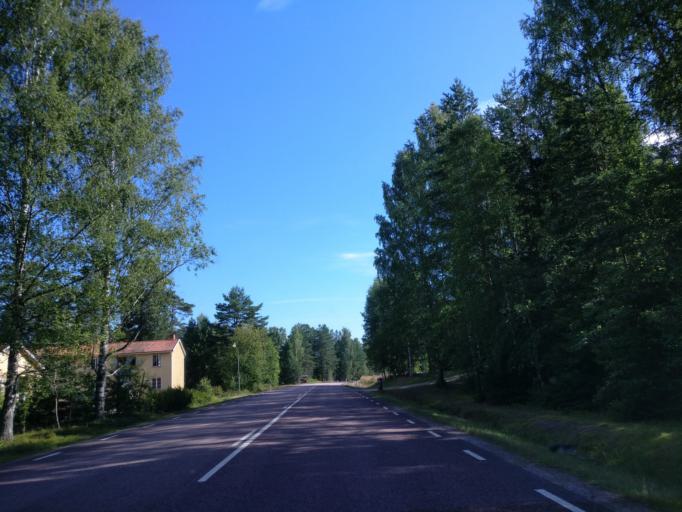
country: SE
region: Vaermland
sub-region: Hagfors Kommun
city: Hagfors
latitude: 60.0641
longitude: 13.7196
